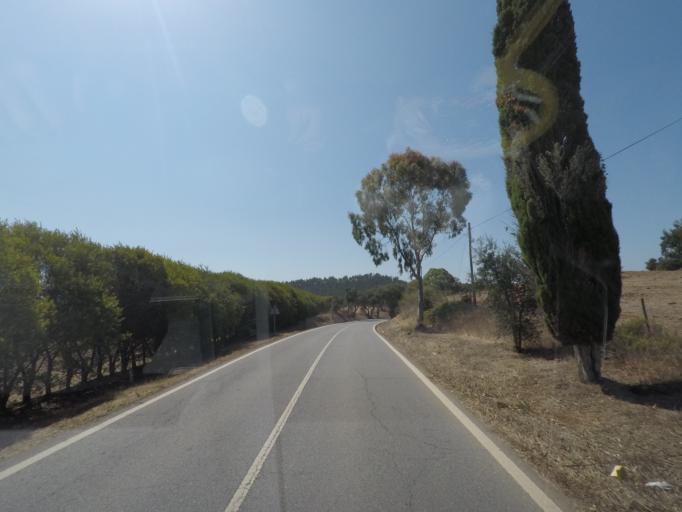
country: PT
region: Beja
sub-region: Odemira
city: Sao Teotonio
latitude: 37.5361
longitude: -8.6919
